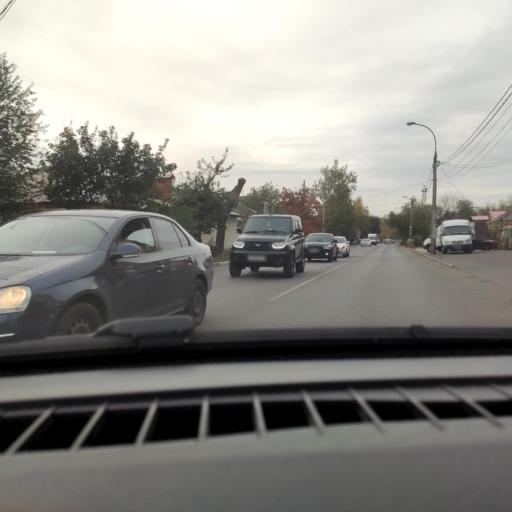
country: RU
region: Voronezj
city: Voronezh
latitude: 51.6664
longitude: 39.1732
